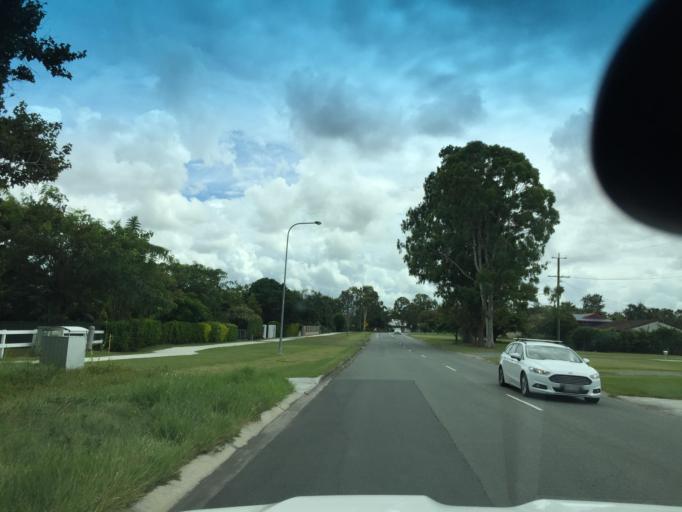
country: AU
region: Queensland
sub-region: Moreton Bay
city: Burpengary
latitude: -27.1344
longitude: 152.9834
